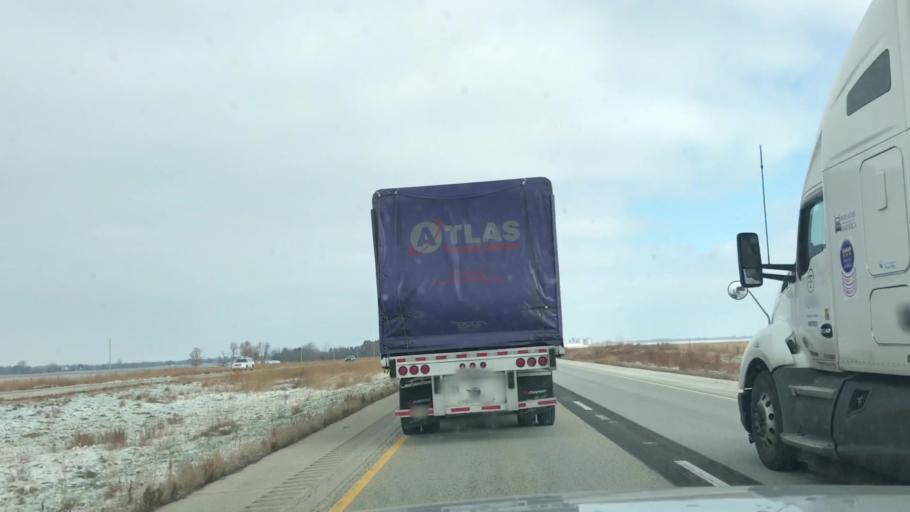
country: US
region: Illinois
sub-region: Sangamon County
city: Divernon
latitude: 39.5326
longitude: -89.6454
